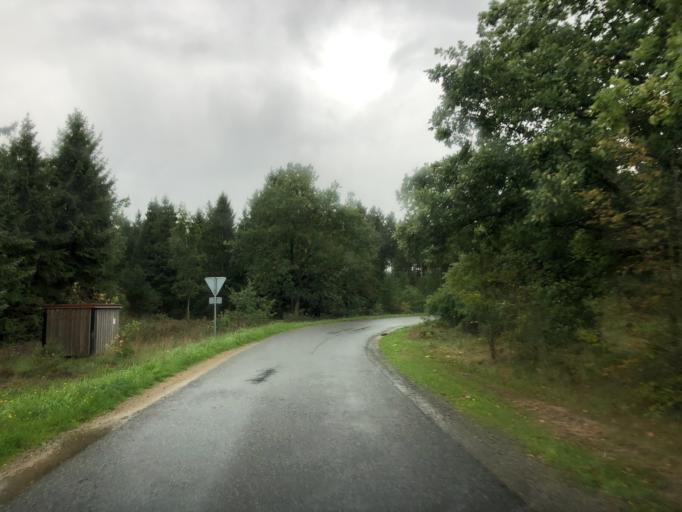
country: DK
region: Central Jutland
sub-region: Ikast-Brande Kommune
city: Brande
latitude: 55.9921
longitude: 9.2107
